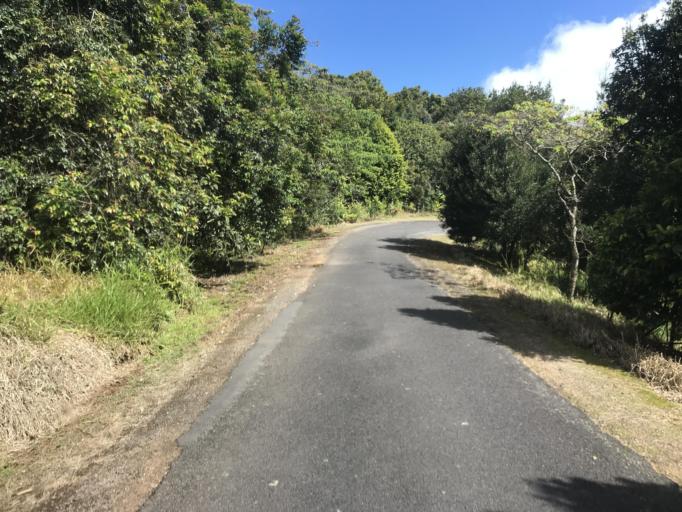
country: AU
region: Queensland
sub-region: Tablelands
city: Ravenshoe
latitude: -17.5204
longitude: 145.5673
